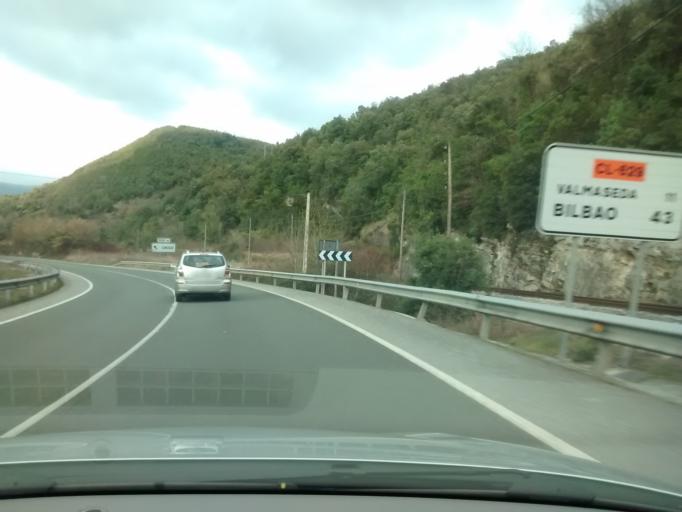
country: ES
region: Castille and Leon
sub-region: Provincia de Burgos
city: Villasana de Mena
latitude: 43.1349
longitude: -3.2621
